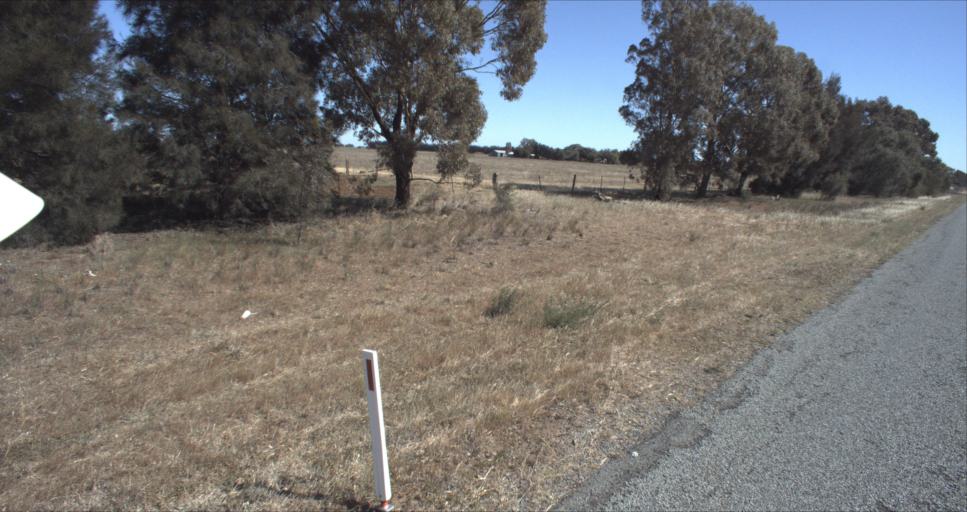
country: AU
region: New South Wales
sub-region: Leeton
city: Leeton
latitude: -34.5348
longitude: 146.3176
